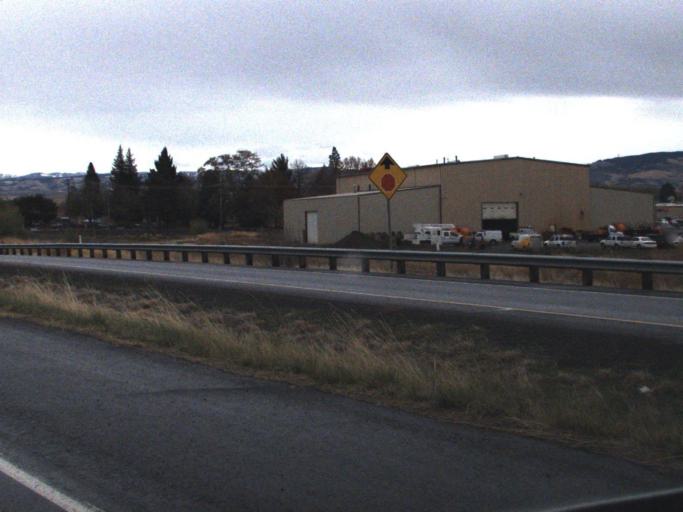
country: US
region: Washington
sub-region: Walla Walla County
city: Walla Walla East
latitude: 46.0835
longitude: -118.2863
